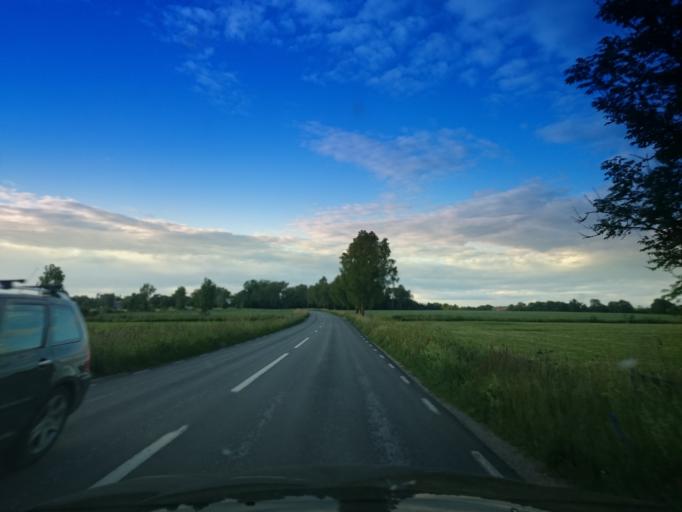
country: SE
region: Gotland
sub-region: Gotland
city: Hemse
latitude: 57.3136
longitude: 18.3831
